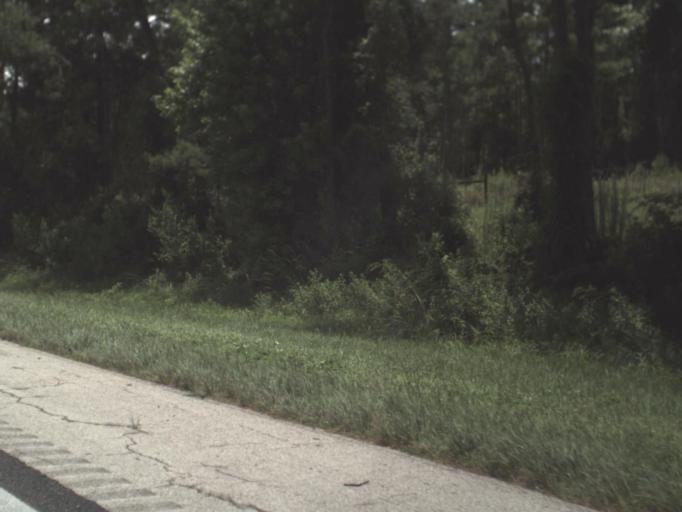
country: US
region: Florida
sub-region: Alachua County
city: Alachua
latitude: 29.7337
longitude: -82.4755
